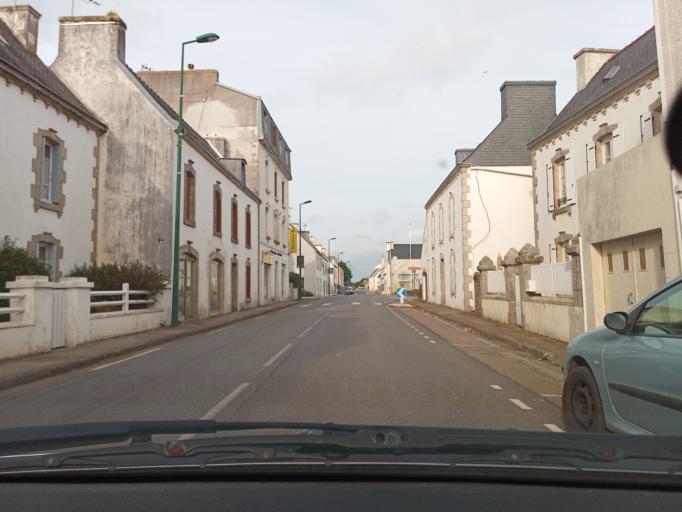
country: FR
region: Brittany
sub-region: Departement du Finistere
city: Plozevet
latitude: 47.9878
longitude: -4.4235
